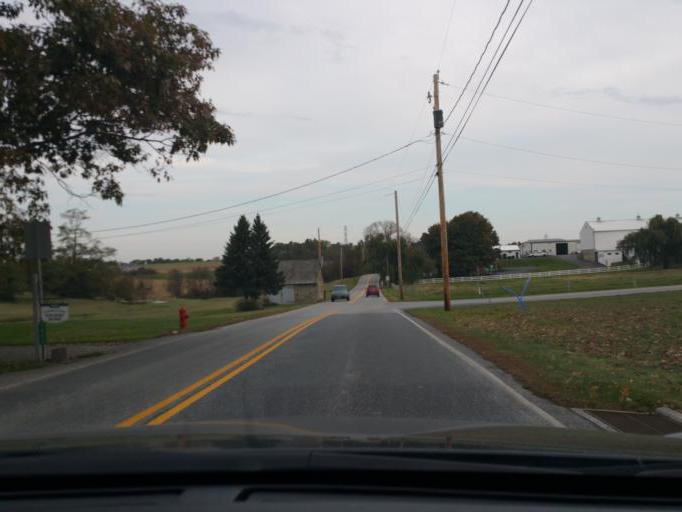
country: US
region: Pennsylvania
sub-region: Lancaster County
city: Willow Street
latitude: 39.9941
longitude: -76.2751
